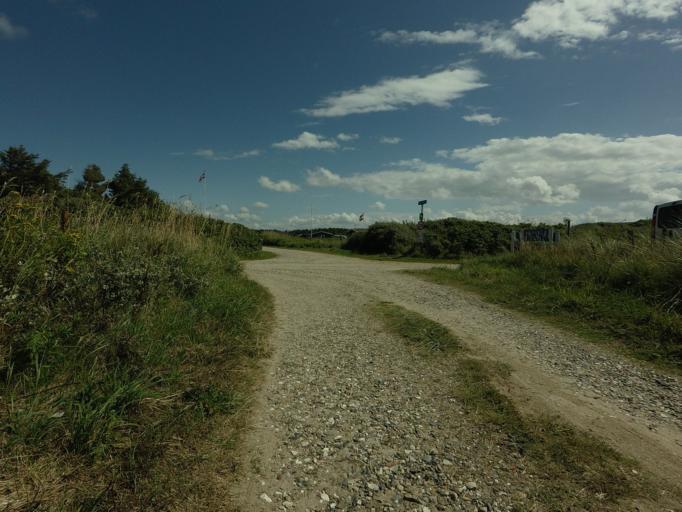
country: DK
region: North Denmark
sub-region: Jammerbugt Kommune
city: Pandrup
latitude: 57.3613
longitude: 9.7004
